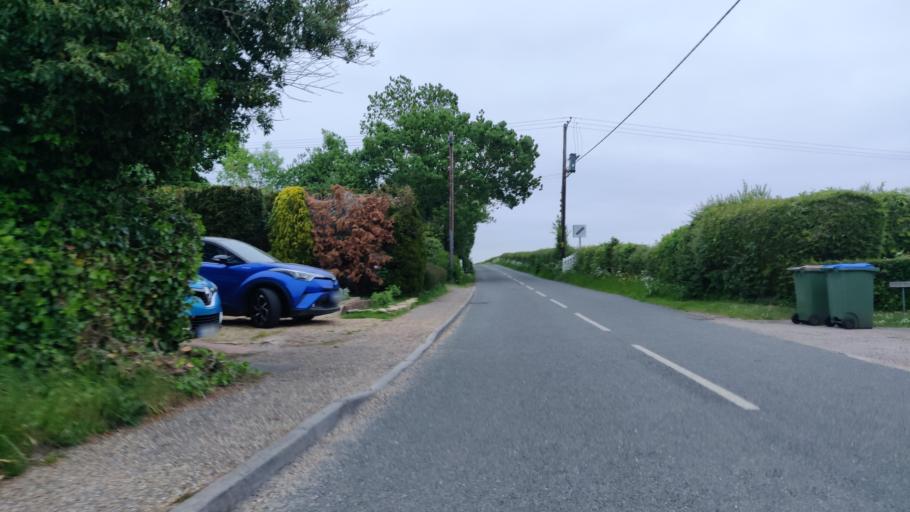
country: GB
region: England
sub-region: West Sussex
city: Partridge Green
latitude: 50.9715
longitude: -0.3025
